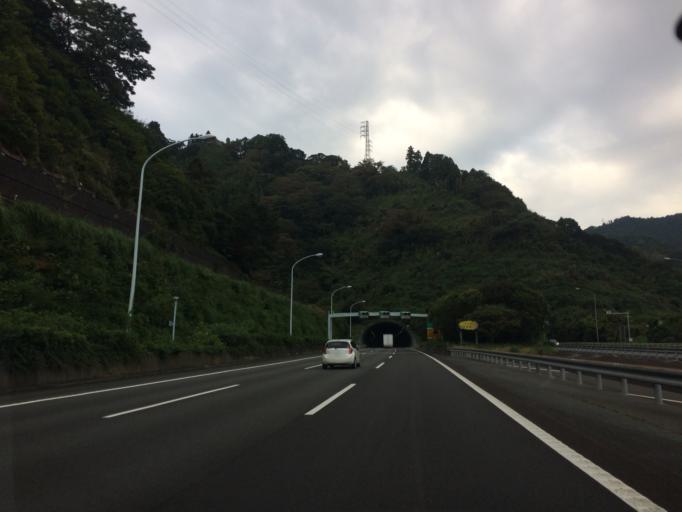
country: JP
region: Shizuoka
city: Yaizu
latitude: 34.9210
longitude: 138.3479
